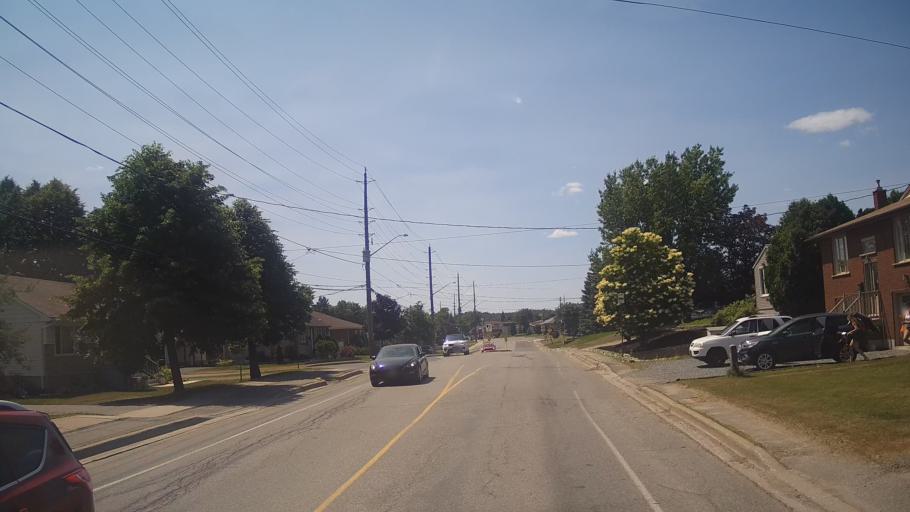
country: CA
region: Ontario
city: Greater Sudbury
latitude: 46.4598
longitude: -81.0235
